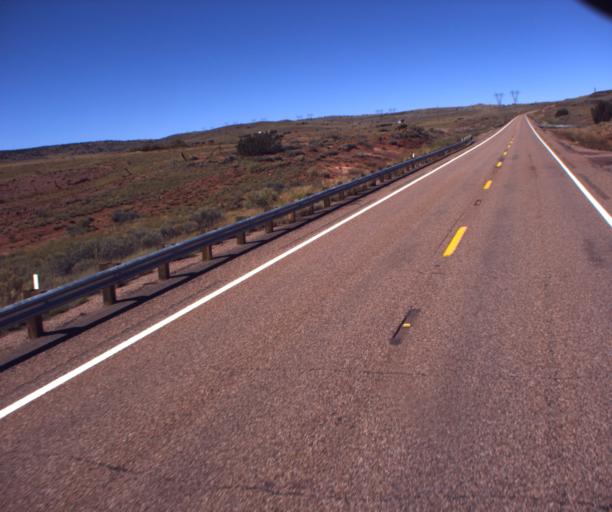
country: US
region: Arizona
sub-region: Apache County
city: Saint Johns
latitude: 34.5454
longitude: -109.4791
